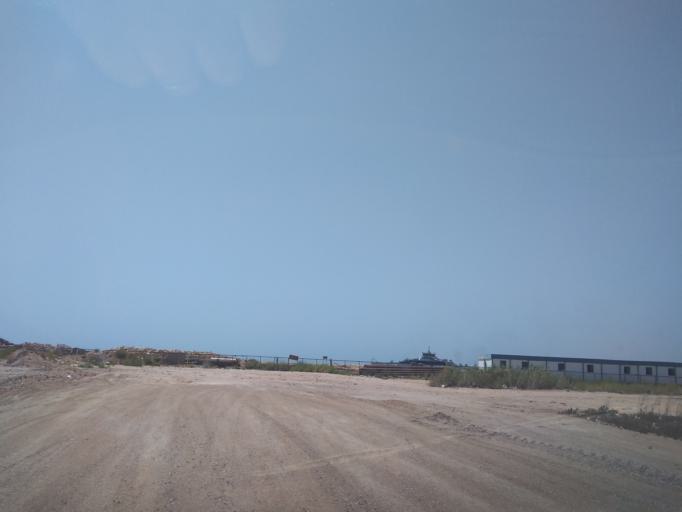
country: TN
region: Safaqis
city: Al Qarmadah
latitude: 34.7242
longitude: 10.7810
